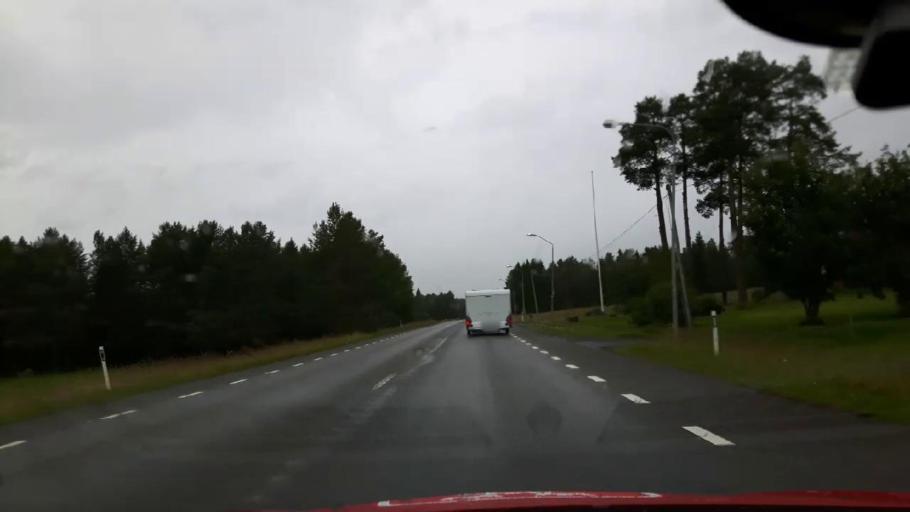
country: SE
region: Jaemtland
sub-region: Are Kommun
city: Jarpen
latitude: 63.3318
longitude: 13.5238
